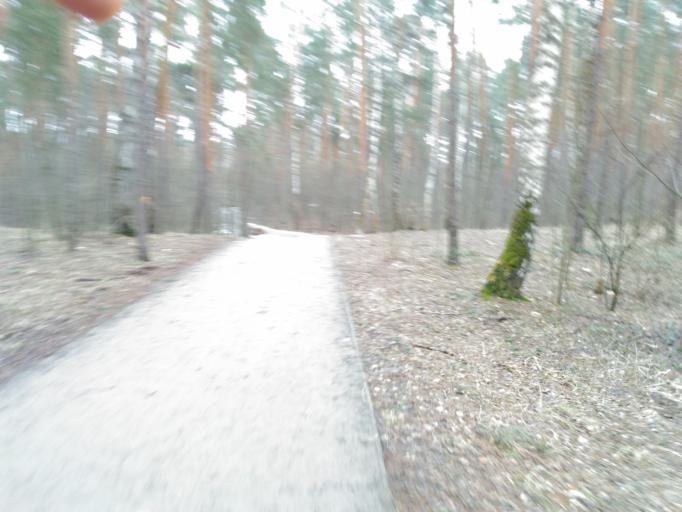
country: RU
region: Moscow
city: Shchukino
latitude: 55.7804
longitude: 37.4190
